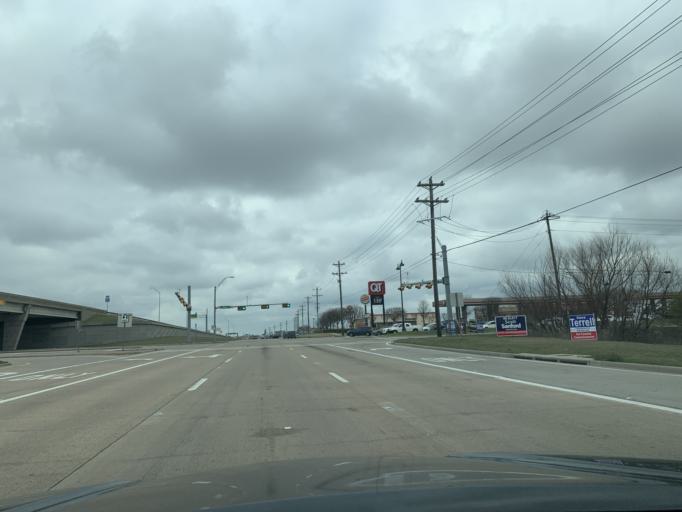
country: US
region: Texas
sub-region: Collin County
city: Allen
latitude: 33.1409
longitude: -96.6910
